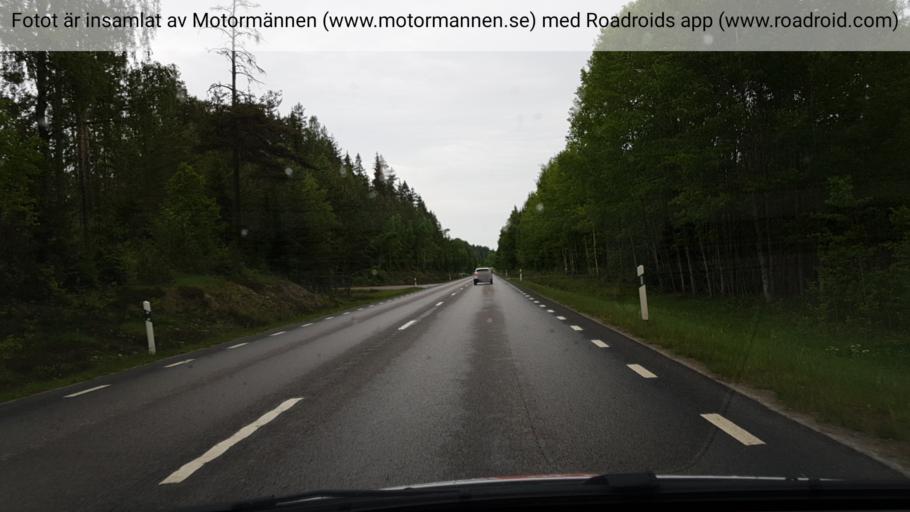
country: SE
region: Kalmar
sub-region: Hultsfreds Kommun
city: Hultsfred
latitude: 57.5447
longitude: 15.8461
